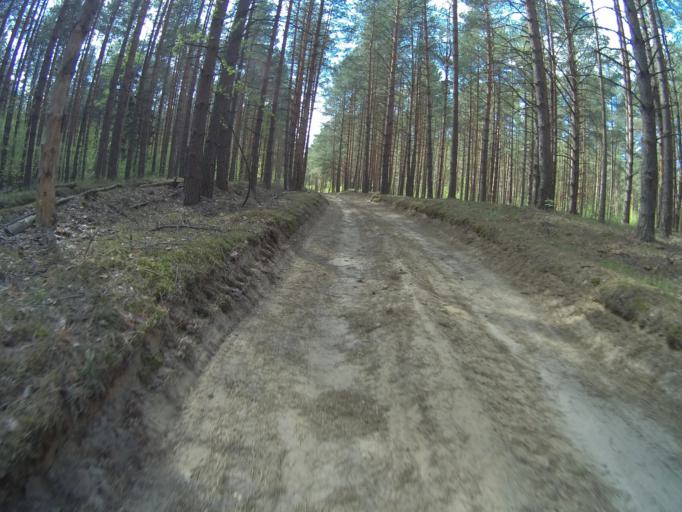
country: RU
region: Vladimir
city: Raduzhnyy
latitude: 56.0174
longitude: 40.2891
